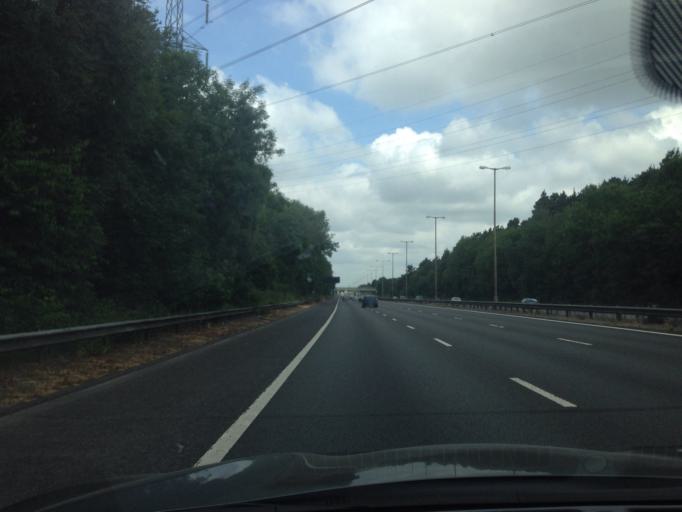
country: GB
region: England
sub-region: Hertfordshire
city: Bushey
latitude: 51.6608
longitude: -0.3483
